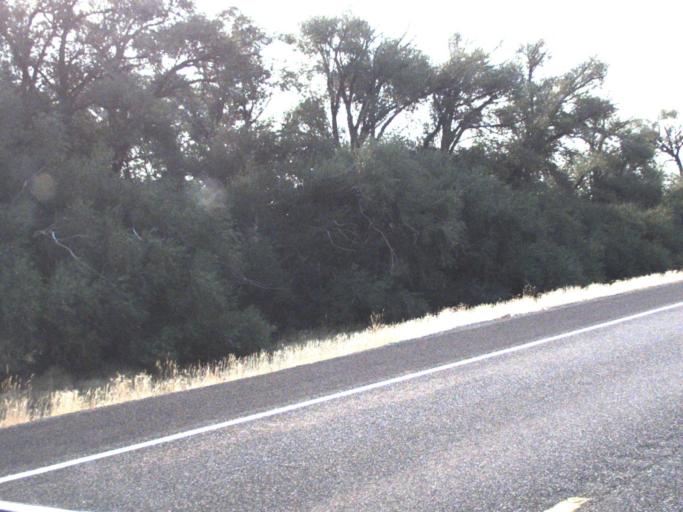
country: US
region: Washington
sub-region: Kittitas County
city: Ellensburg
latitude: 47.0656
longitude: -120.6234
